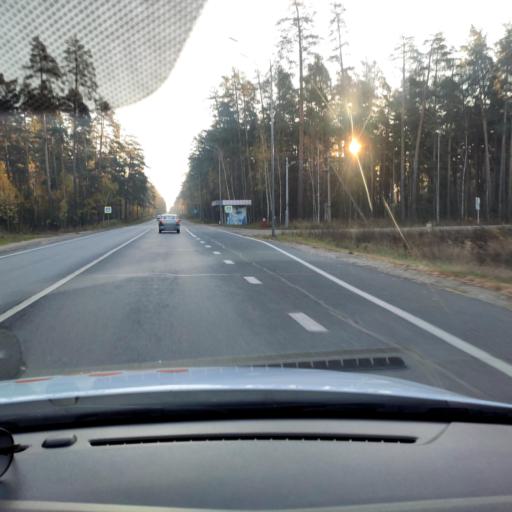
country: RU
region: Tatarstan
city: Stolbishchi
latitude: 55.6365
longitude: 49.0623
